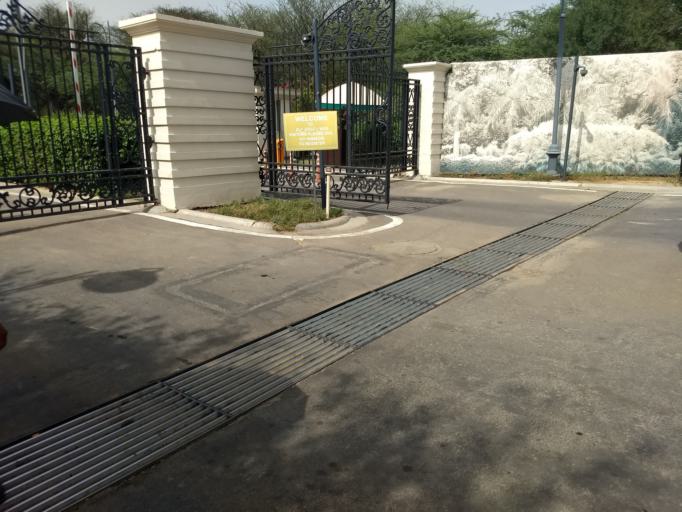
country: IN
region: Haryana
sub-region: Gurgaon
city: Gurgaon
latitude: 28.4502
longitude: 77.1063
